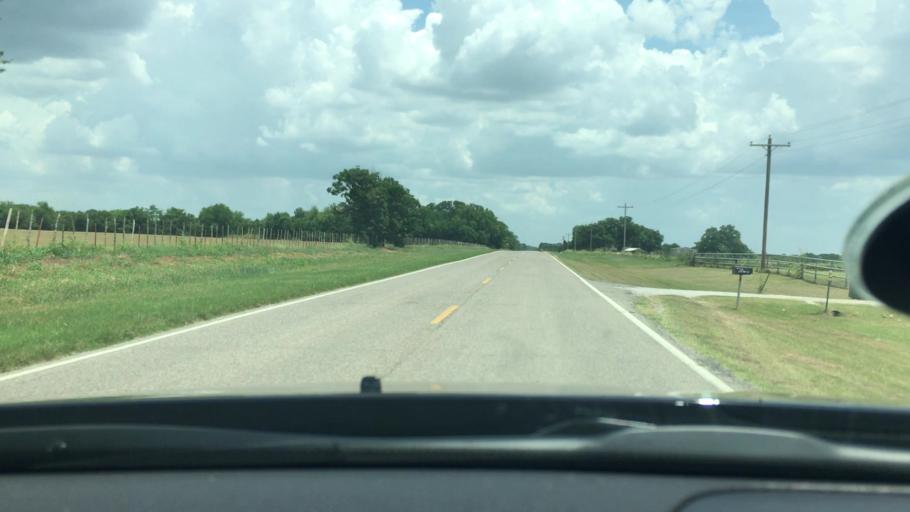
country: US
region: Oklahoma
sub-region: Love County
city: Marietta
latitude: 33.9839
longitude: -96.9496
